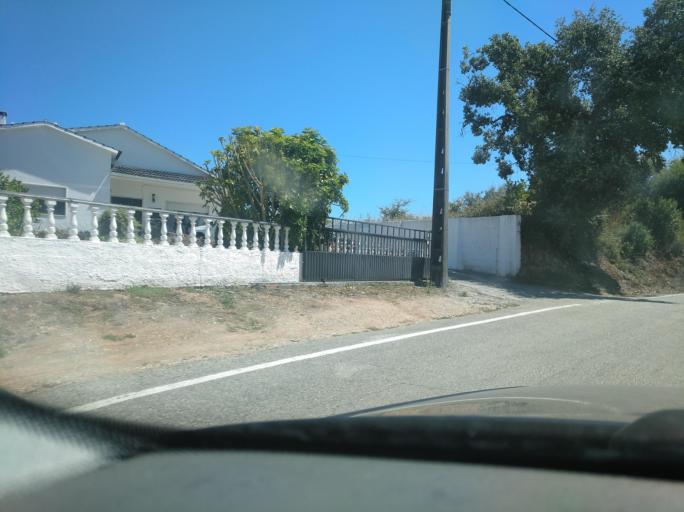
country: PT
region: Leiria
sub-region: Alcobaca
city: Aljubarrota
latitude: 39.5690
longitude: -8.9338
